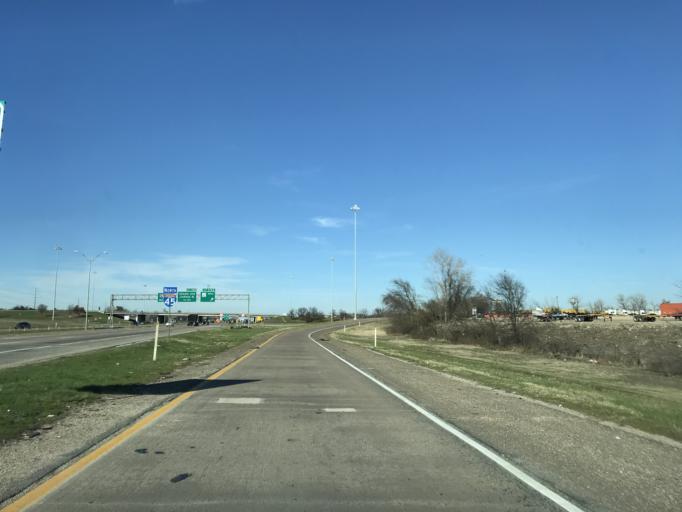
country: US
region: Texas
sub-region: Dallas County
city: Hutchins
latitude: 32.6970
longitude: -96.7512
